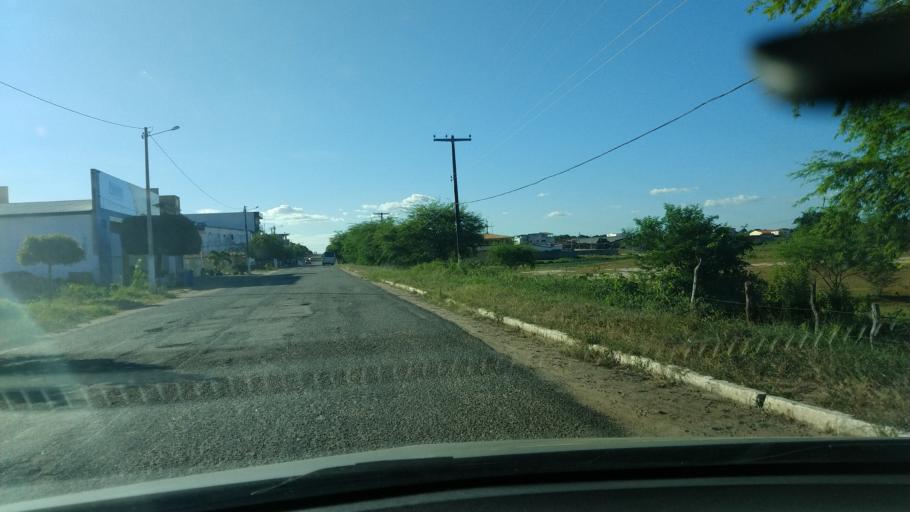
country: BR
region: Rio Grande do Norte
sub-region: Sao Jose Do Campestre
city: Sao Jose do Campestre
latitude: -6.4398
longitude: -35.6421
